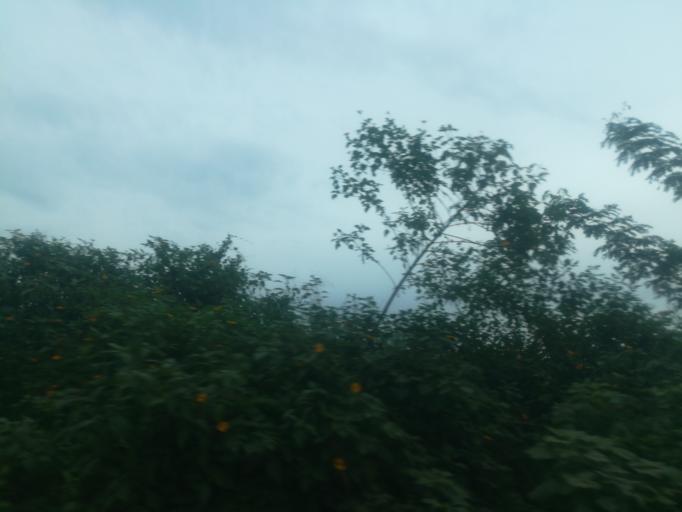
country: NG
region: Oyo
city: Egbeda
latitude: 7.3824
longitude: 4.0098
